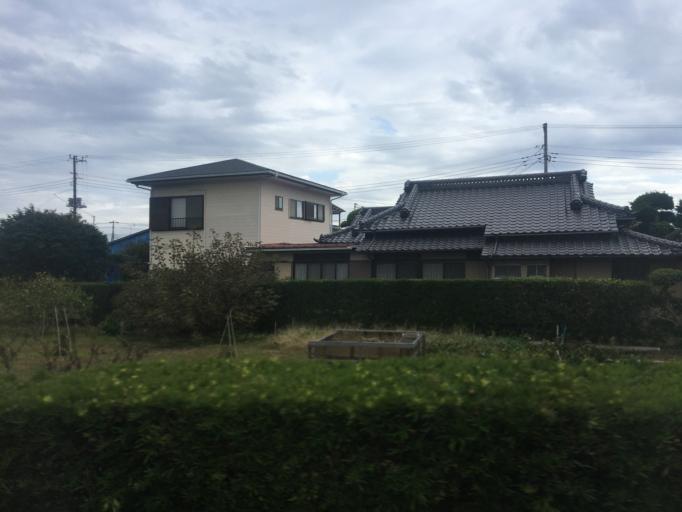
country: JP
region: Chiba
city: Kawaguchi
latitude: 35.0277
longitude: 139.9933
